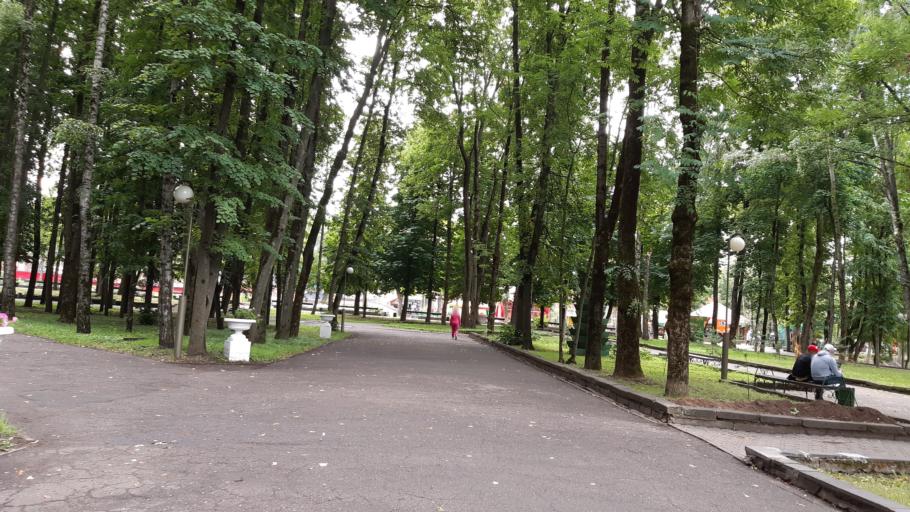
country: RU
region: Smolensk
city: Smolensk
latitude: 54.7832
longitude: 32.0401
